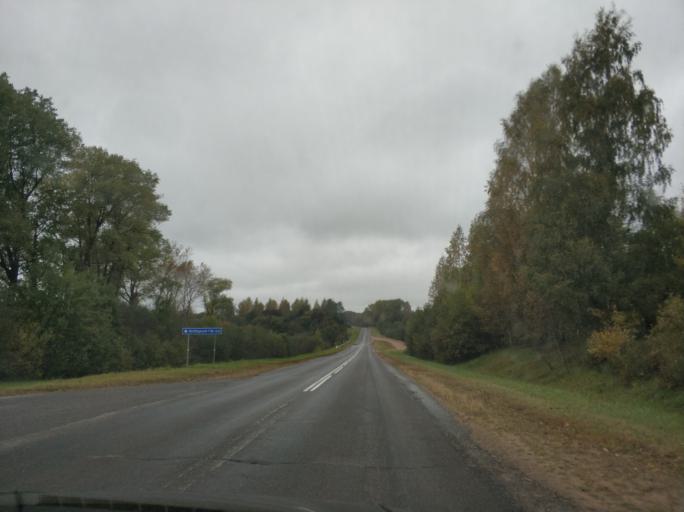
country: BY
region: Vitebsk
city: Polatsk
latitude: 55.4409
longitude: 28.9565
